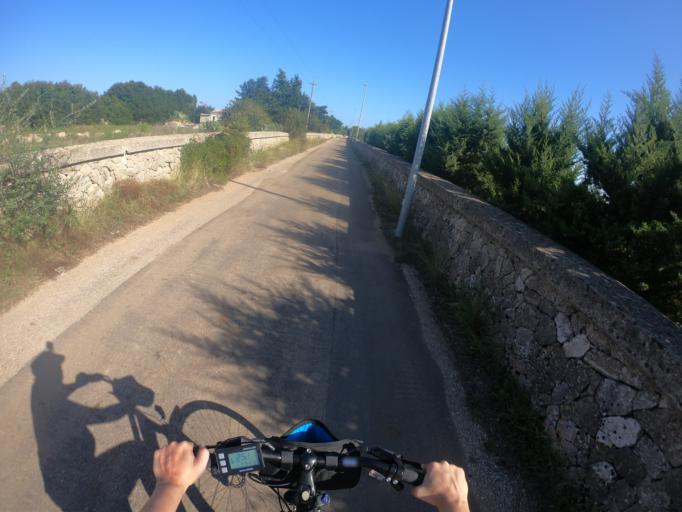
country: IT
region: Apulia
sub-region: Provincia di Lecce
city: Alessano
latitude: 39.8867
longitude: 18.3258
